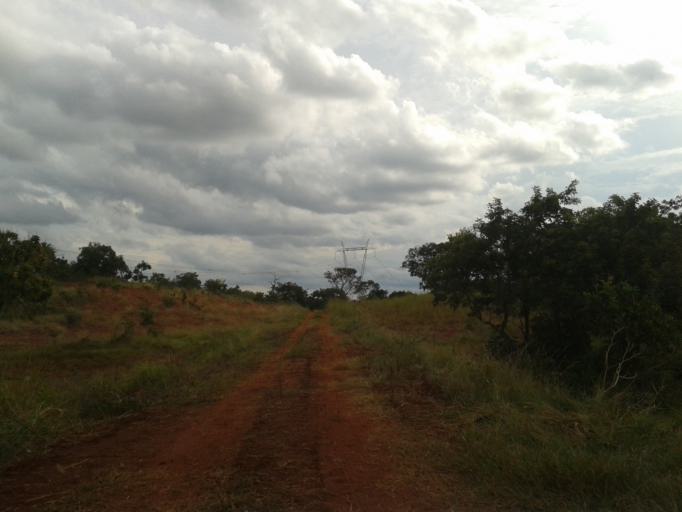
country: BR
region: Minas Gerais
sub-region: Campina Verde
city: Campina Verde
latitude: -19.4396
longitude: -49.5925
